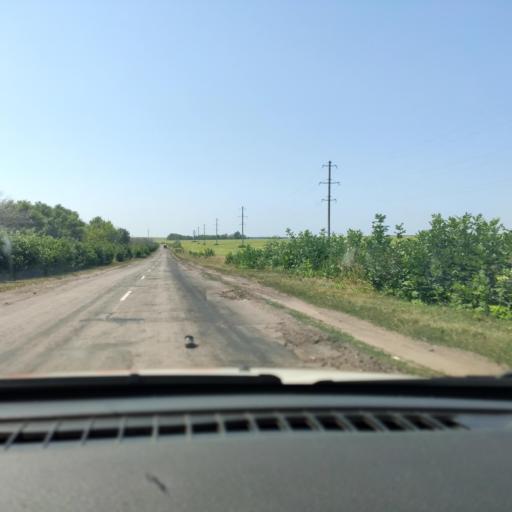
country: RU
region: Voronezj
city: Ol'khovatka
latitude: 50.6016
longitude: 39.3061
